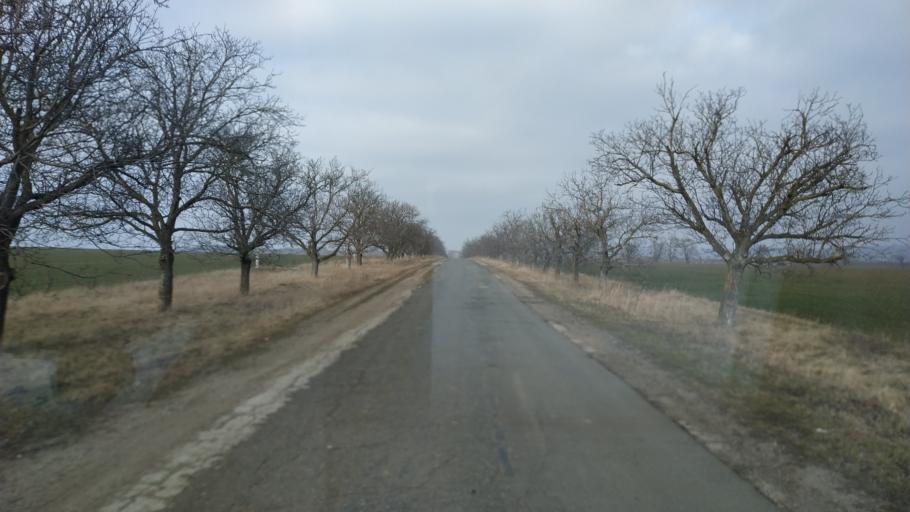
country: MD
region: Hincesti
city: Dancu
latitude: 46.8660
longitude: 28.2925
